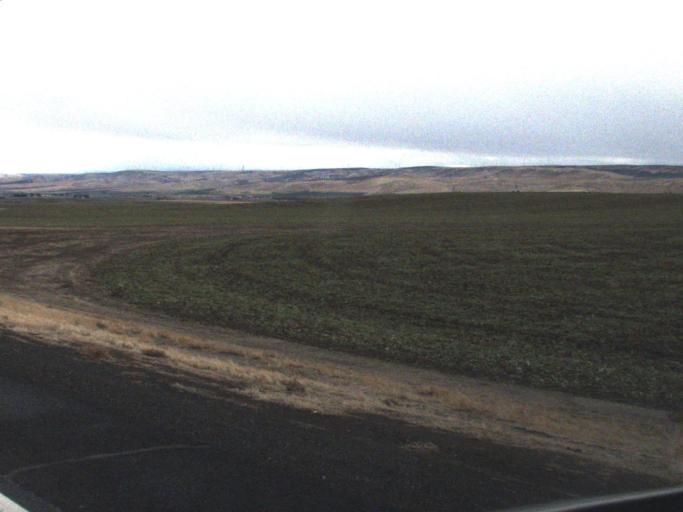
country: US
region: Washington
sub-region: Walla Walla County
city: Burbank
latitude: 46.0614
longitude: -118.7399
